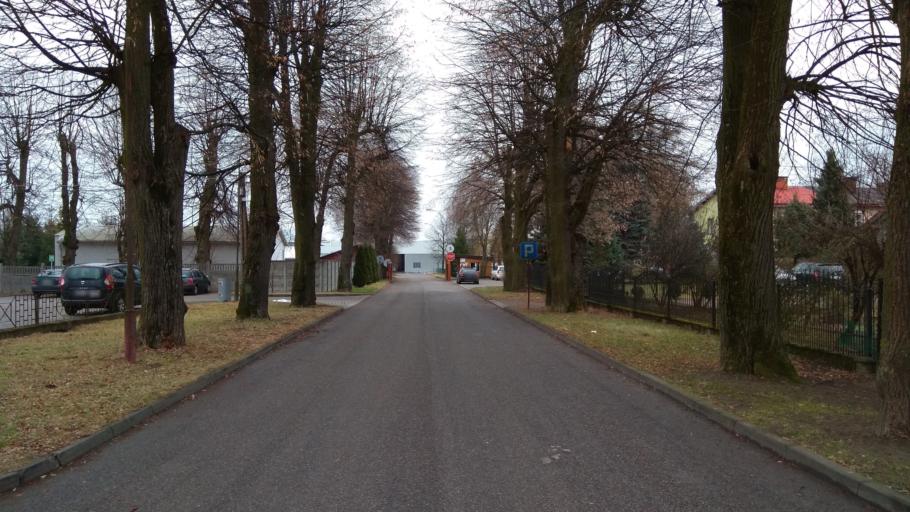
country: PL
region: Subcarpathian Voivodeship
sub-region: Powiat lubaczowski
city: Lubaczow
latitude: 50.1975
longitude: 23.1132
